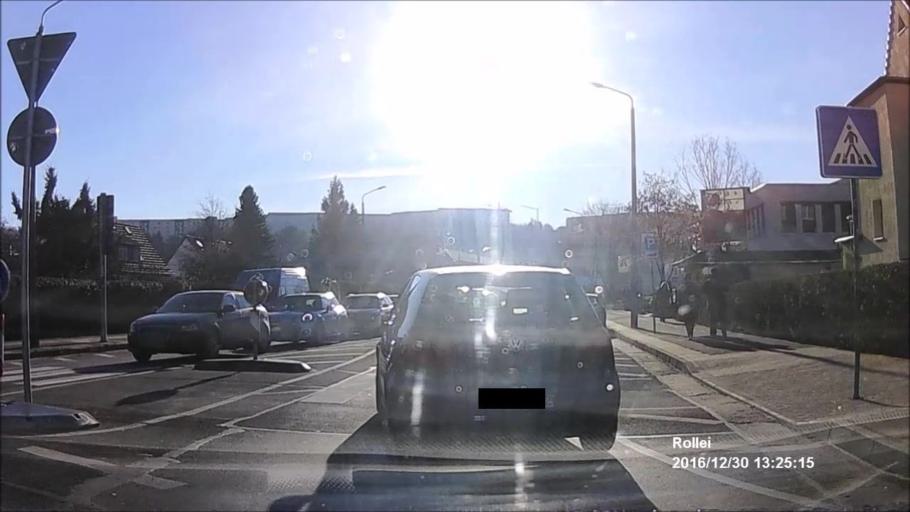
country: DE
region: Thuringia
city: Erfurt
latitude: 50.9579
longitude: 11.0629
